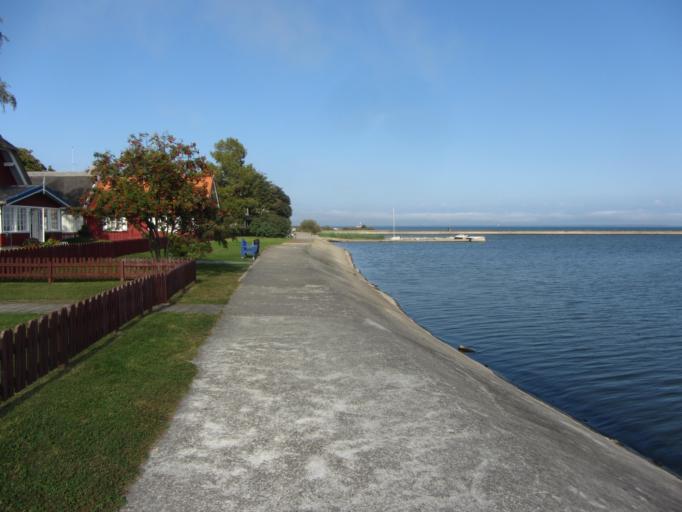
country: LT
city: Neringa
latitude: 55.4130
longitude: 21.0954
